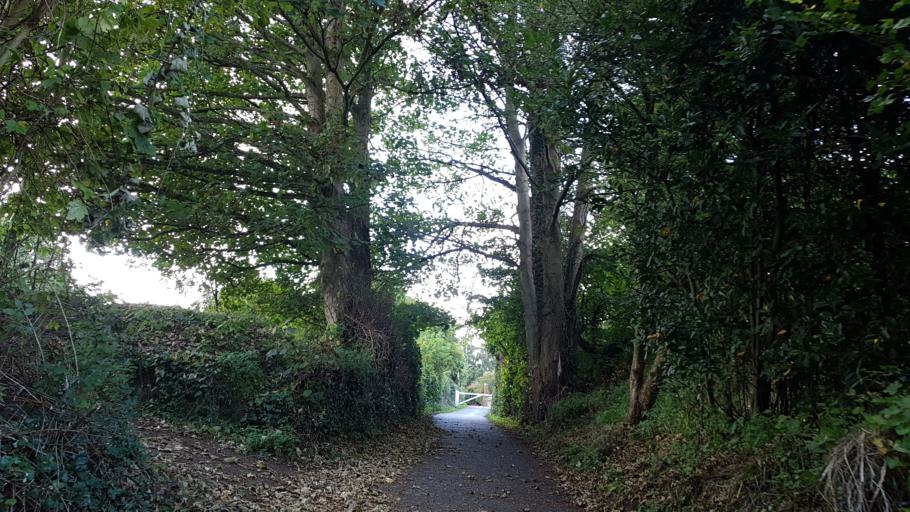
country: GB
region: England
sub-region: Isle of Wight
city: Ryde
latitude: 50.7317
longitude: -1.1842
